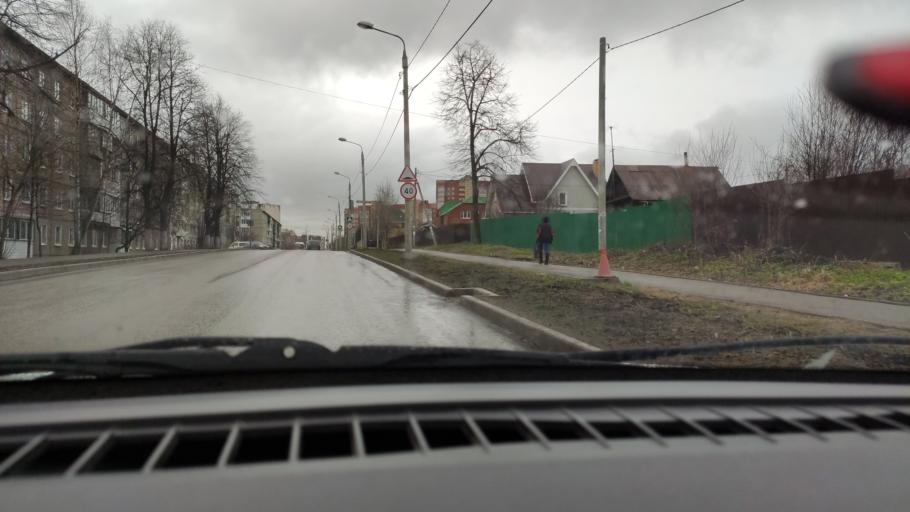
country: RU
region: Perm
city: Perm
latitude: 58.1054
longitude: 56.2962
